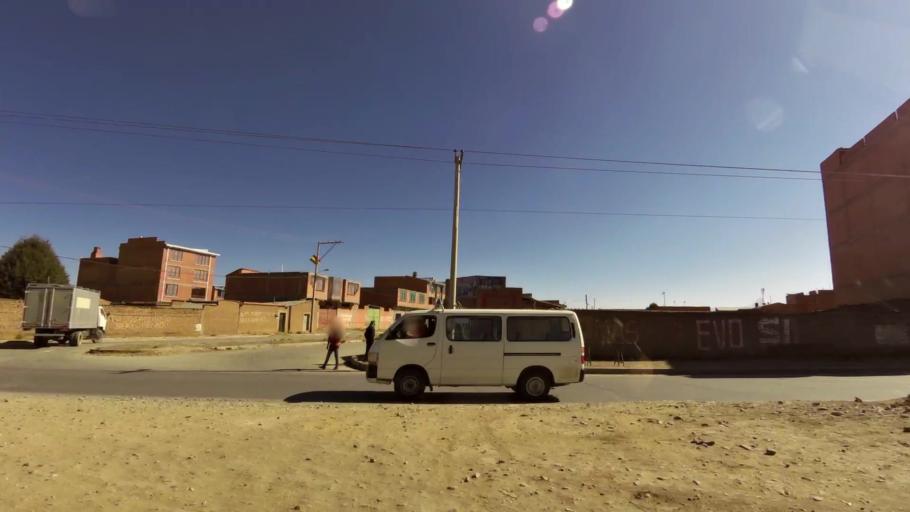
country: BO
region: La Paz
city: La Paz
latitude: -16.5362
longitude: -68.2208
